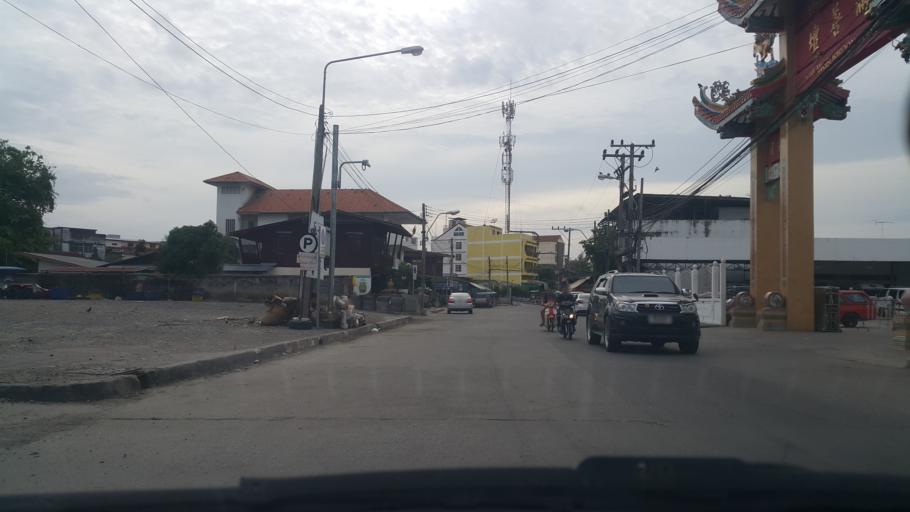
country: TH
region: Chon Buri
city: Phatthaya
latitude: 12.9717
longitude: 100.9083
